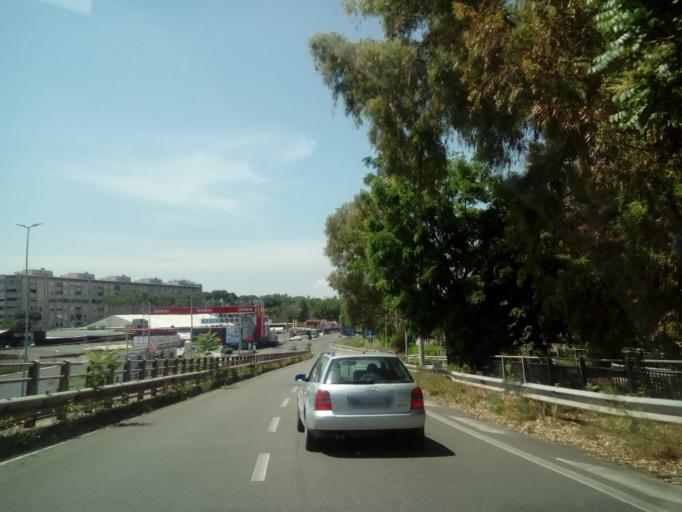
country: IT
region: Latium
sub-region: Citta metropolitana di Roma Capitale
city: Rome
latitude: 41.9185
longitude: 12.5643
